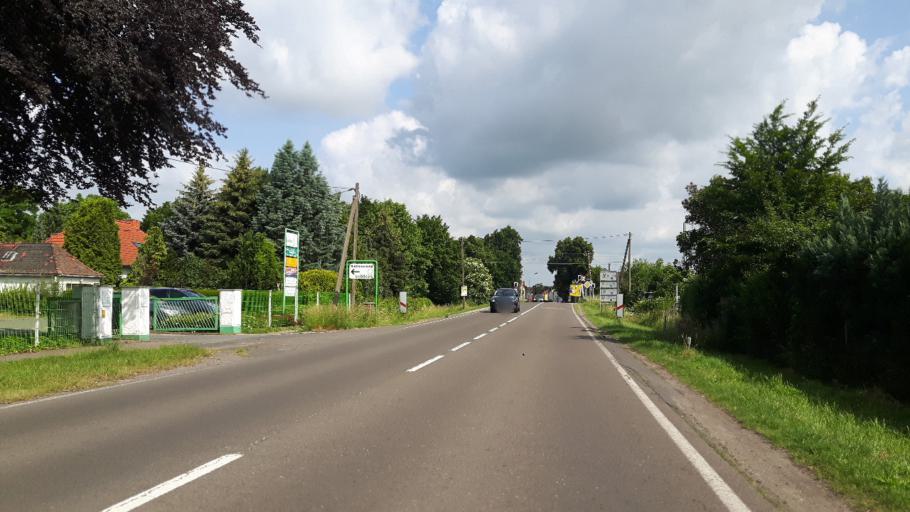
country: DE
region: Saxony
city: Delitzsch
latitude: 51.5198
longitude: 12.3366
